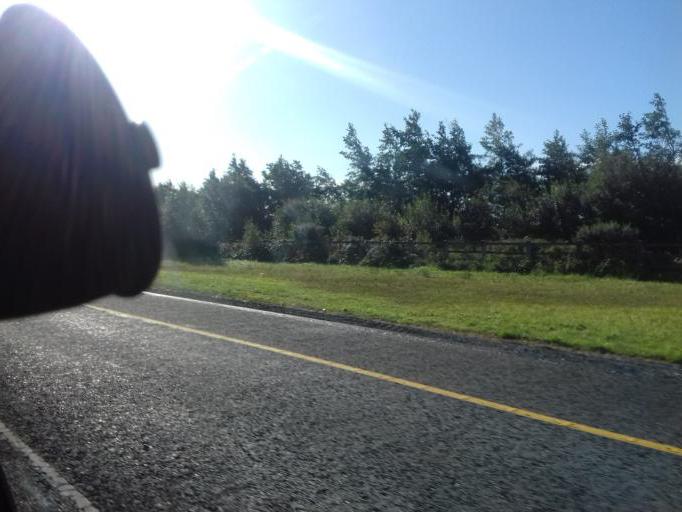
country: IE
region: Leinster
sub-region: An Iarmhi
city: Kinnegad
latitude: 53.4438
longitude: -7.0481
